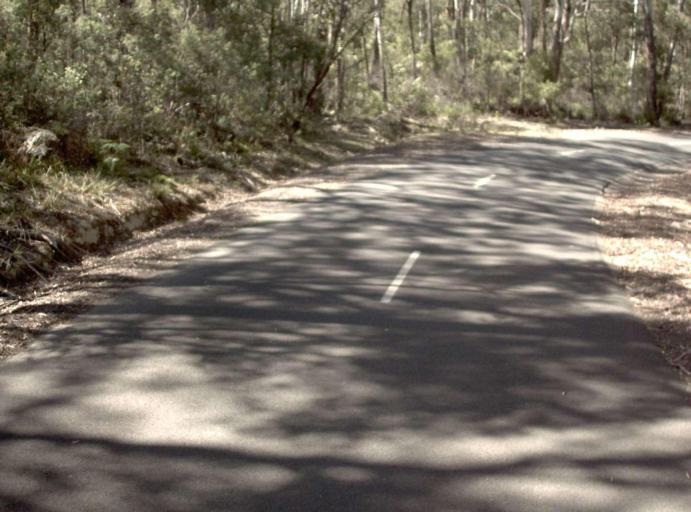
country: AU
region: New South Wales
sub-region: Bombala
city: Bombala
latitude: -37.1141
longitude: 148.7547
